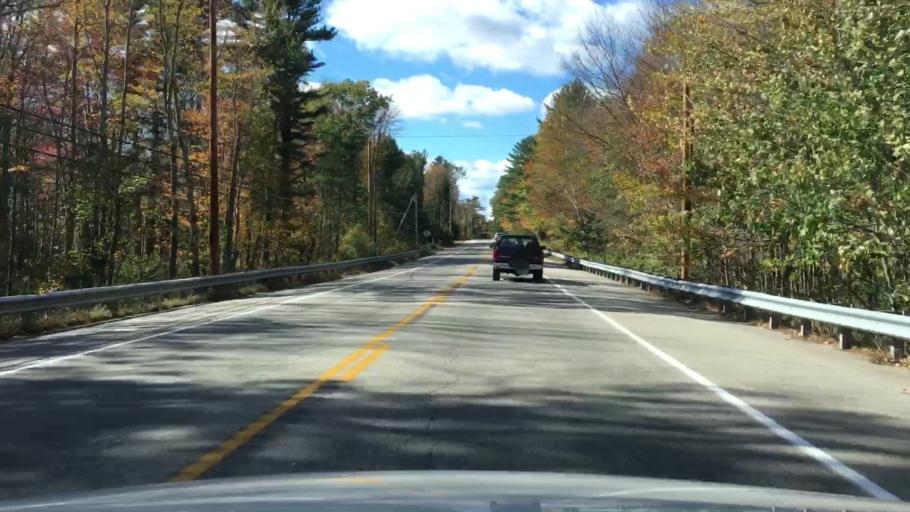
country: US
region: Maine
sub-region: York County
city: Alfred
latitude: 43.4764
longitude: -70.6771
